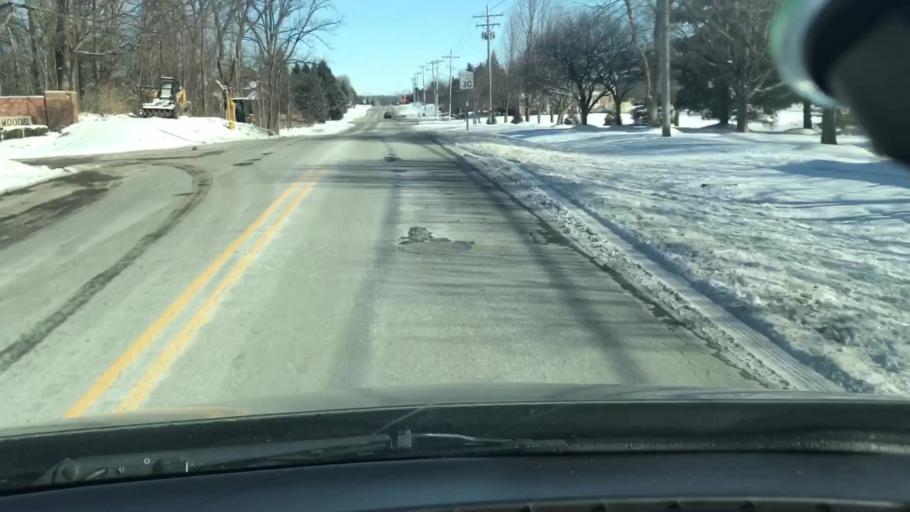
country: US
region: Indiana
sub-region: Hamilton County
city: Carmel
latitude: 39.9712
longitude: -86.0777
